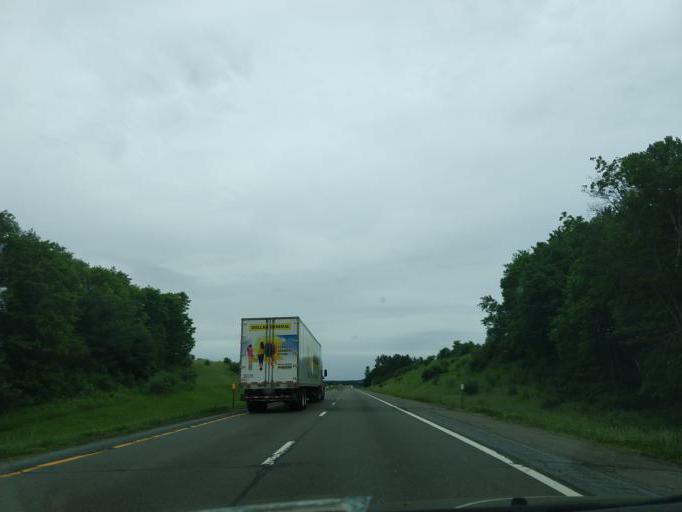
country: US
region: New York
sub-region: Broome County
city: Chenango Bridge
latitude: 42.2455
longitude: -75.9181
